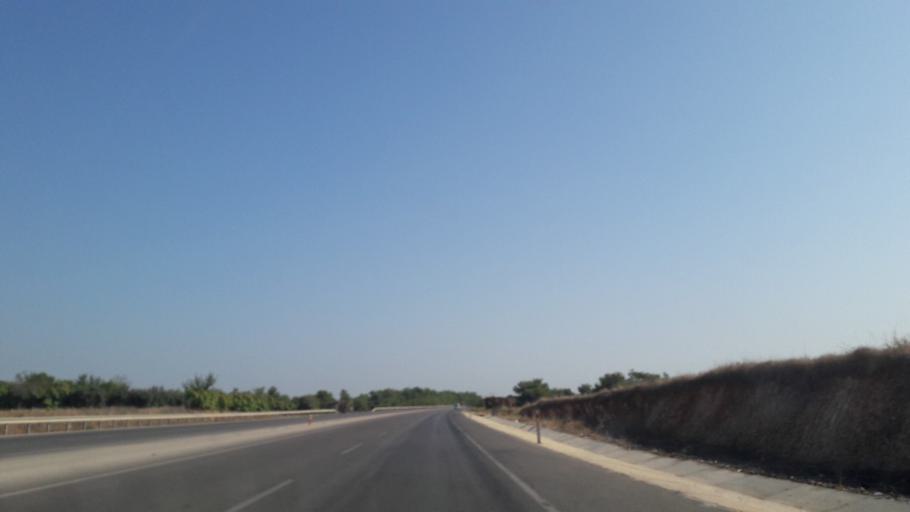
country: TR
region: Adana
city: Sagkaya
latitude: 37.1239
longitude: 35.5175
